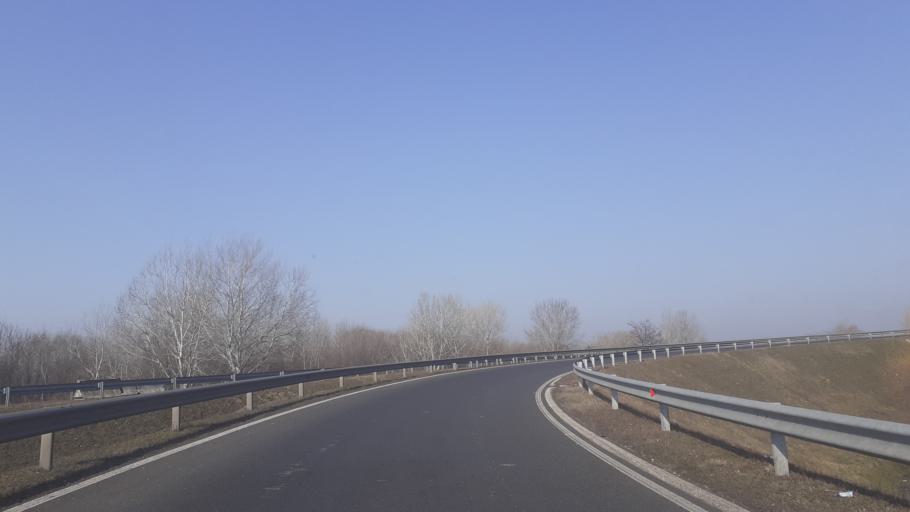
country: HU
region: Fejer
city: Baracs
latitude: 46.9212
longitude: 18.8932
